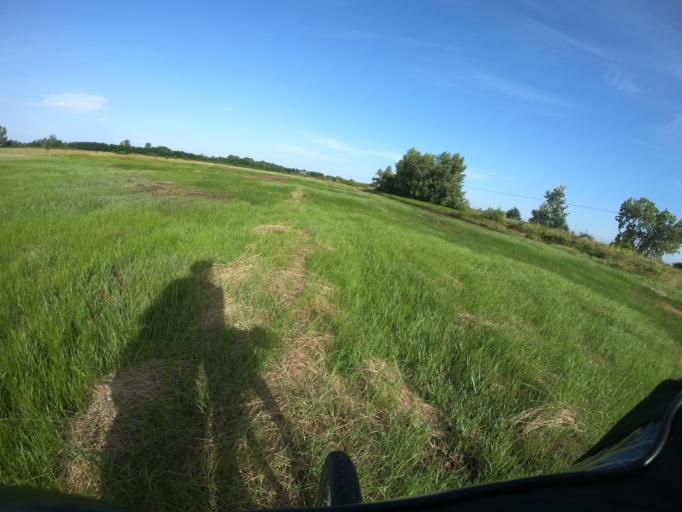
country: HU
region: Hajdu-Bihar
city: Tiszacsege
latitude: 47.6148
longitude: 21.0186
